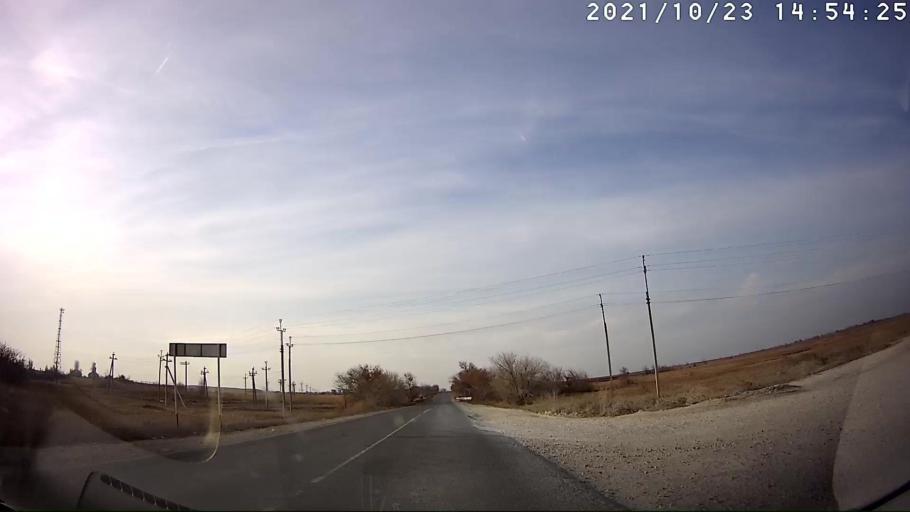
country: RU
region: Volgograd
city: Volgograd
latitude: 48.4479
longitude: 44.4165
